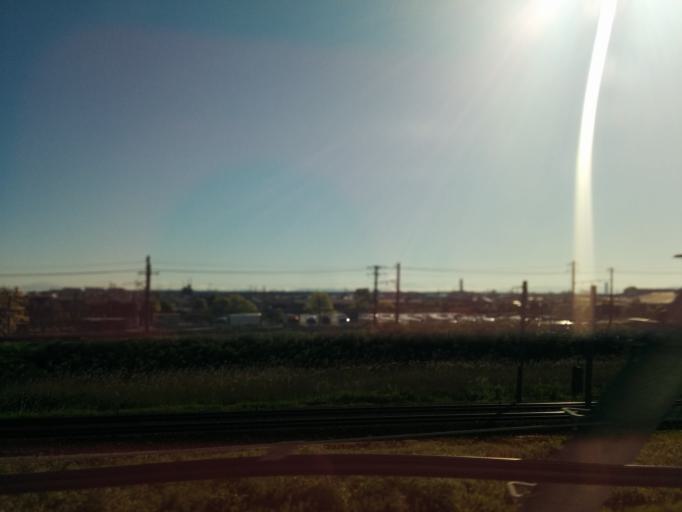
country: JP
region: Aichi
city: Nagoya-shi
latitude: 35.2130
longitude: 136.8450
